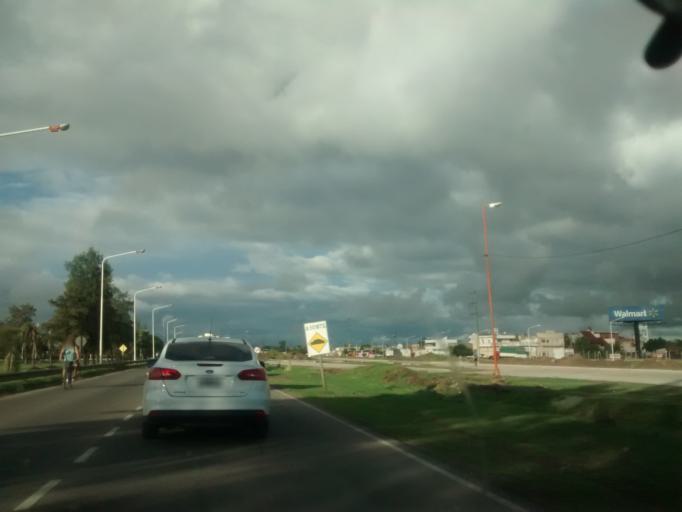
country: AR
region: Chaco
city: Fontana
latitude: -27.4460
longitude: -59.0238
